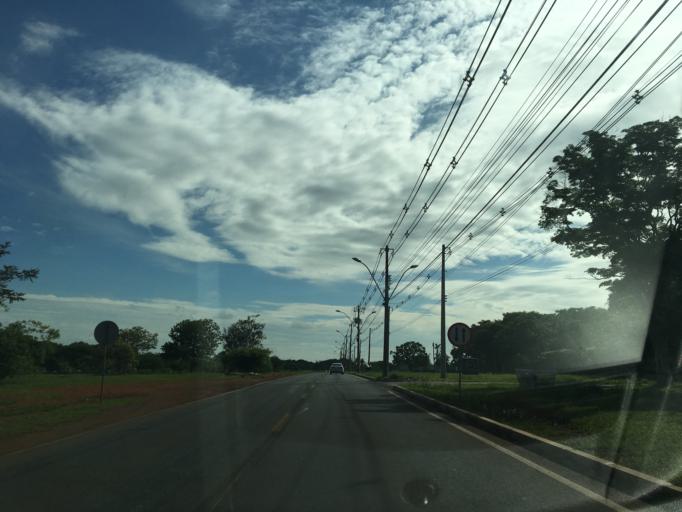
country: BR
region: Federal District
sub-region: Brasilia
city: Brasilia
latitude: -15.8683
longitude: -47.9431
